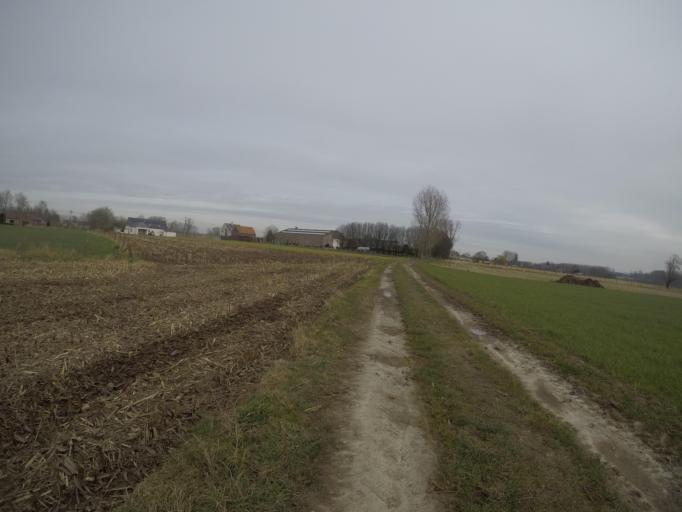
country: BE
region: Flanders
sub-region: Provincie Oost-Vlaanderen
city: Sint-Maria-Lierde
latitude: 50.8004
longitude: 3.8346
